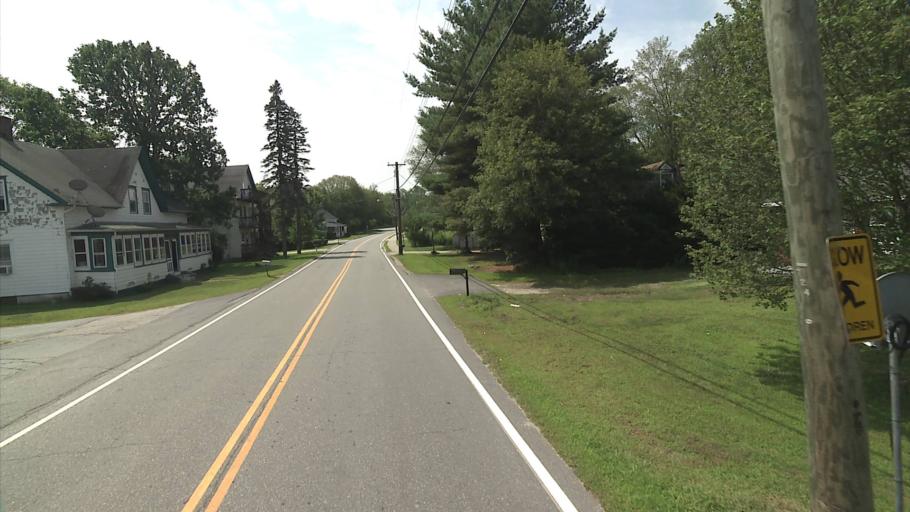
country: US
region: Connecticut
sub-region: Windham County
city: Moosup
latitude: 41.7204
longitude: -71.8732
